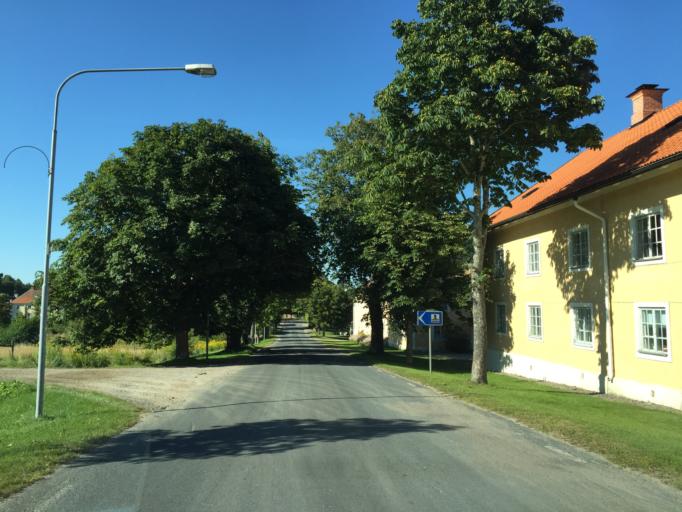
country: SE
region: OErebro
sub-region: Orebro Kommun
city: Odensbacken
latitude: 59.0102
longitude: 15.5831
